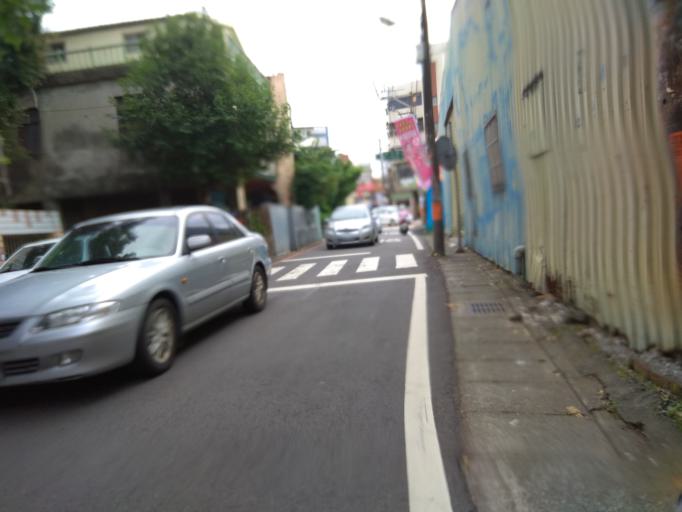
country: TW
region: Taiwan
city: Daxi
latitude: 24.9411
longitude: 121.2059
